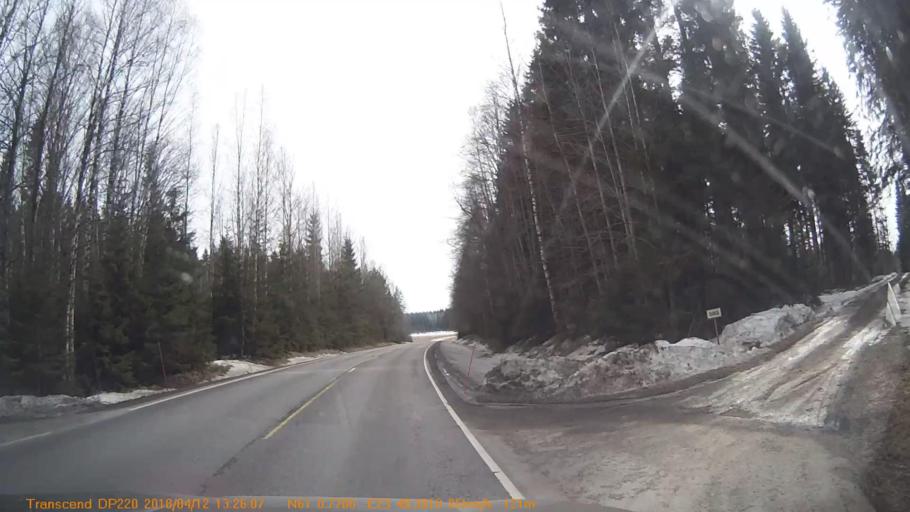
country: FI
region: Pirkanmaa
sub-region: Etelae-Pirkanmaa
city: Kylmaekoski
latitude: 61.0127
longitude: 23.6733
